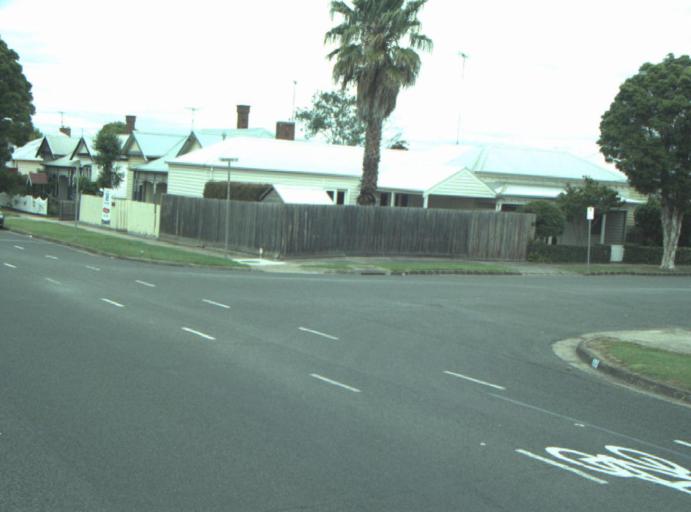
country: AU
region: Victoria
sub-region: Greater Geelong
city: East Geelong
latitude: -38.1585
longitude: 144.3641
